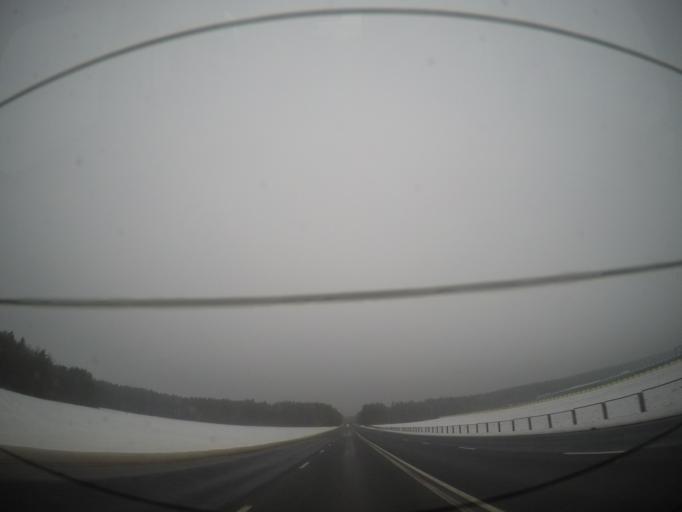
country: BY
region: Grodnenskaya
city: Hrodna
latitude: 53.6215
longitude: 23.8761
